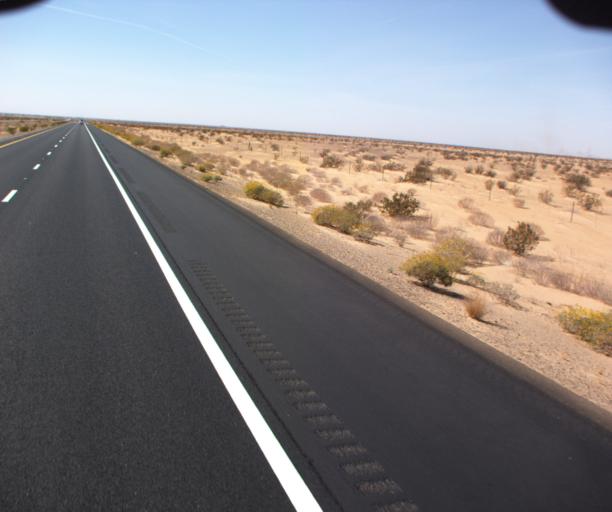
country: US
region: Arizona
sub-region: Yuma County
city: Somerton
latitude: 32.4954
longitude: -114.5909
